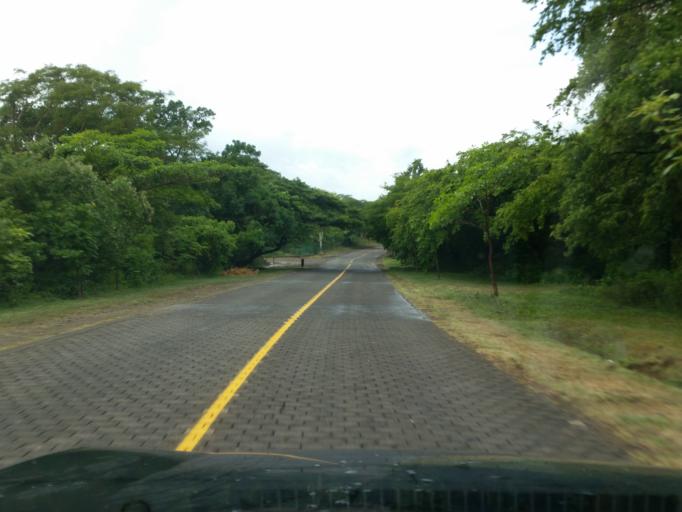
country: NI
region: Managua
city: Masachapa
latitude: 11.8154
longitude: -86.4968
